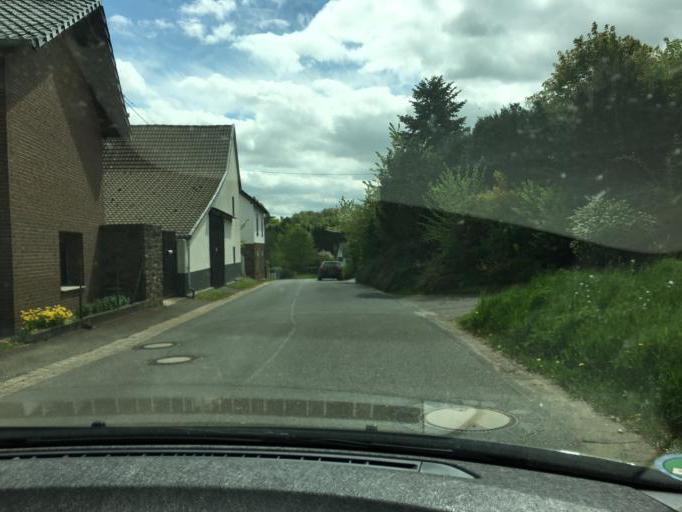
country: DE
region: Rheinland-Pfalz
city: Kirchsahr
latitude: 50.5189
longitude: 6.8620
